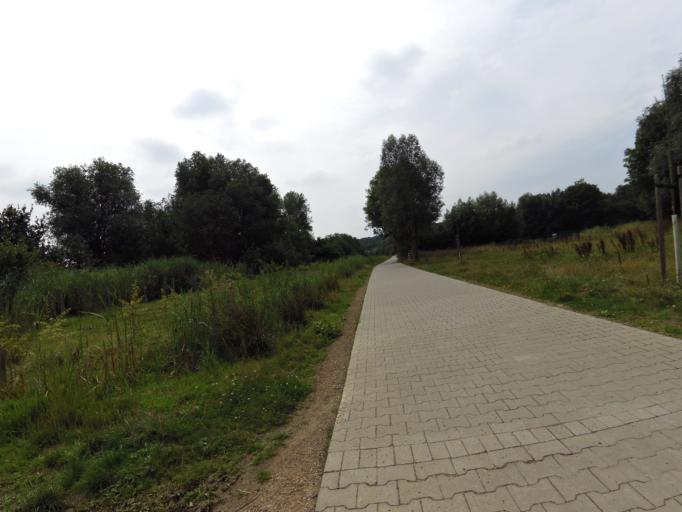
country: DE
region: North Rhine-Westphalia
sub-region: Regierungsbezirk Koln
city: Ubach-Palenberg
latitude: 50.9336
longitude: 6.0975
